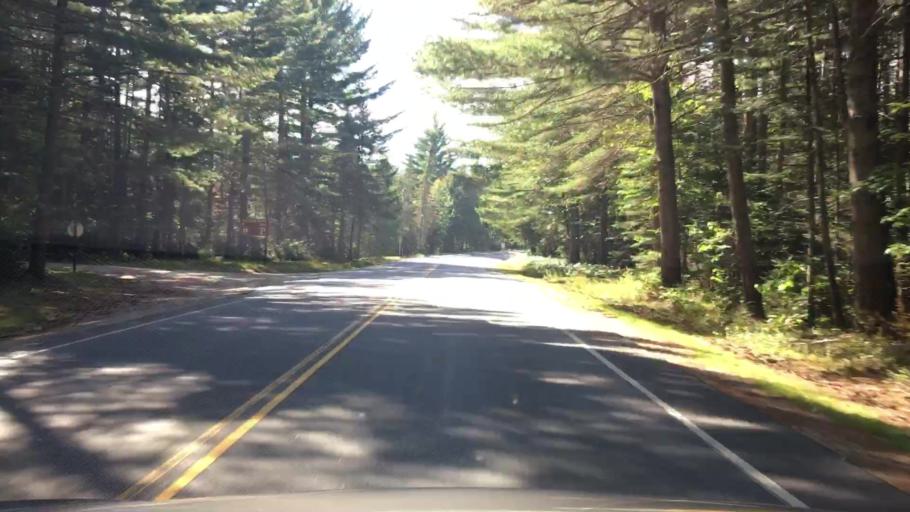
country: US
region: New Hampshire
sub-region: Carroll County
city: Tamworth
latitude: 43.9962
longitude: -71.3497
